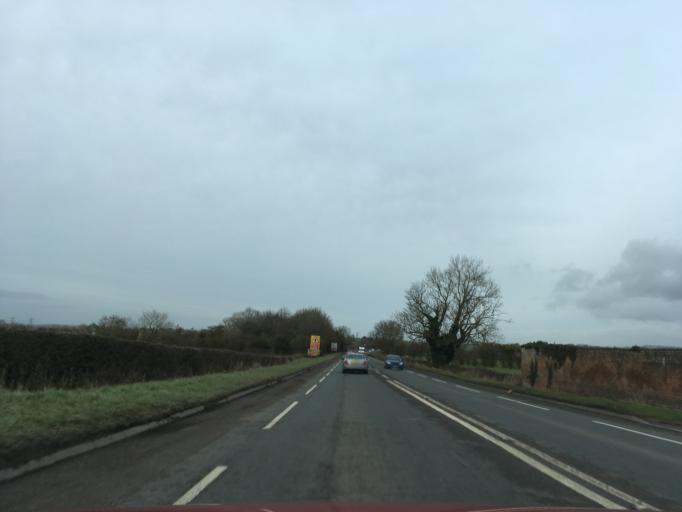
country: GB
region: England
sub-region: Gloucestershire
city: Stonehouse
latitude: 51.7546
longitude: -2.3409
